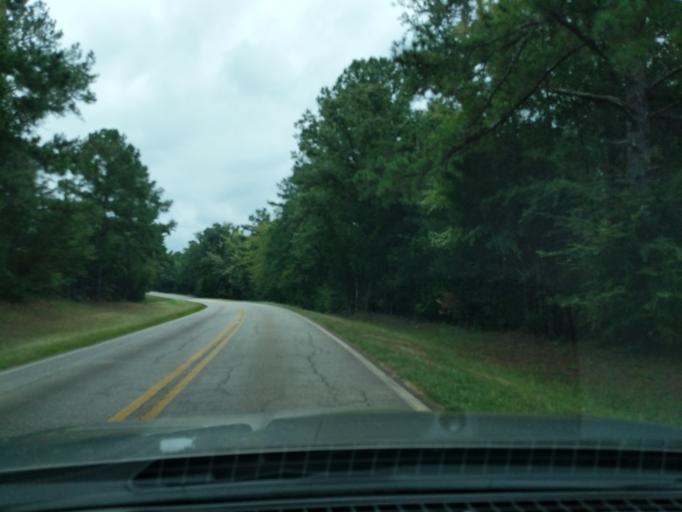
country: US
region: Georgia
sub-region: Columbia County
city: Appling
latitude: 33.5847
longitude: -82.3751
